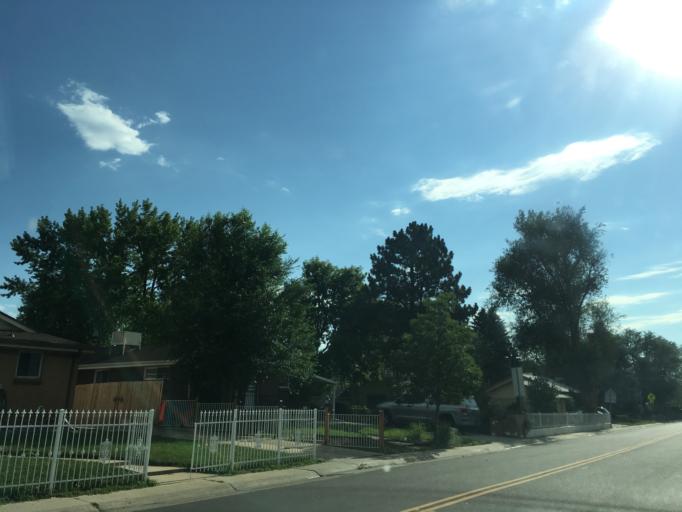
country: US
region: Colorado
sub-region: Arapahoe County
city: Sheridan
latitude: 39.6931
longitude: -105.0333
